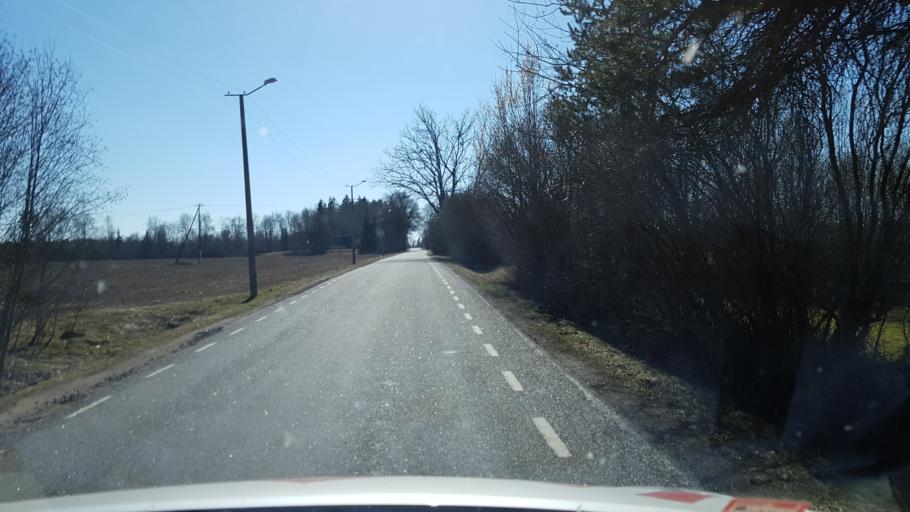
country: EE
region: Laeaene-Virumaa
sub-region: Tamsalu vald
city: Tamsalu
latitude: 59.0861
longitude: 26.1640
